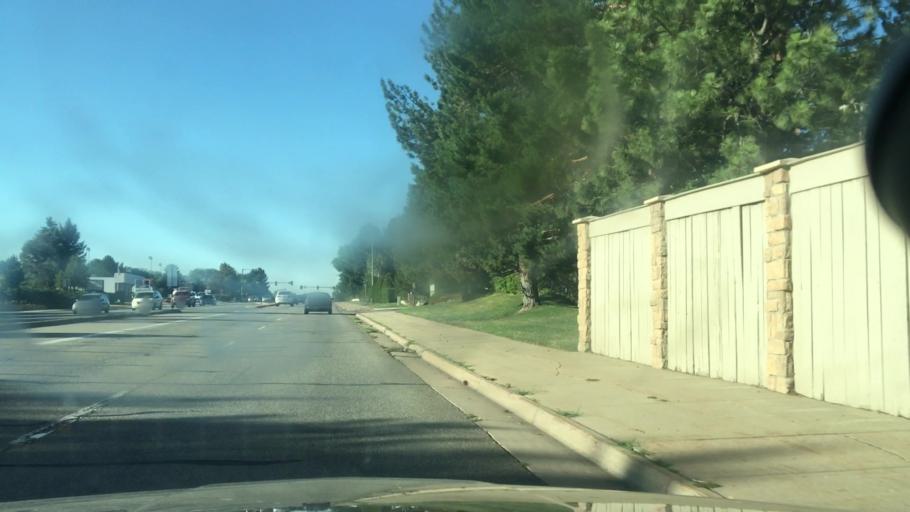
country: US
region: Colorado
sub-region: Arapahoe County
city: Castlewood
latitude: 39.6341
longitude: -104.8853
